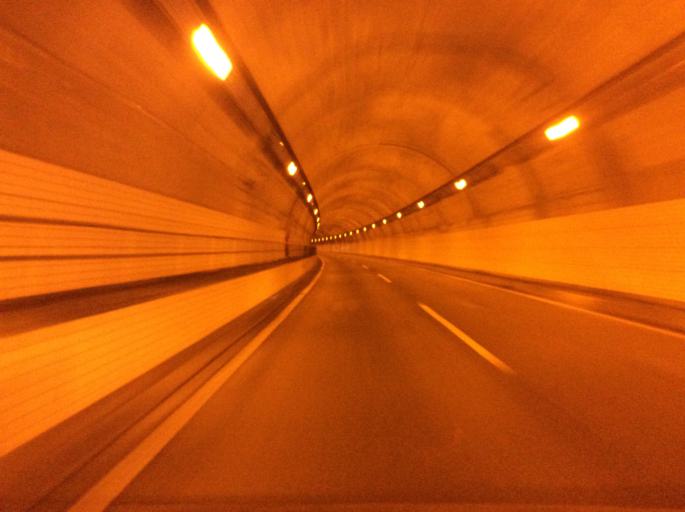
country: JP
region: Ibaraki
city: Hitachi
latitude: 36.6149
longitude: 140.6368
